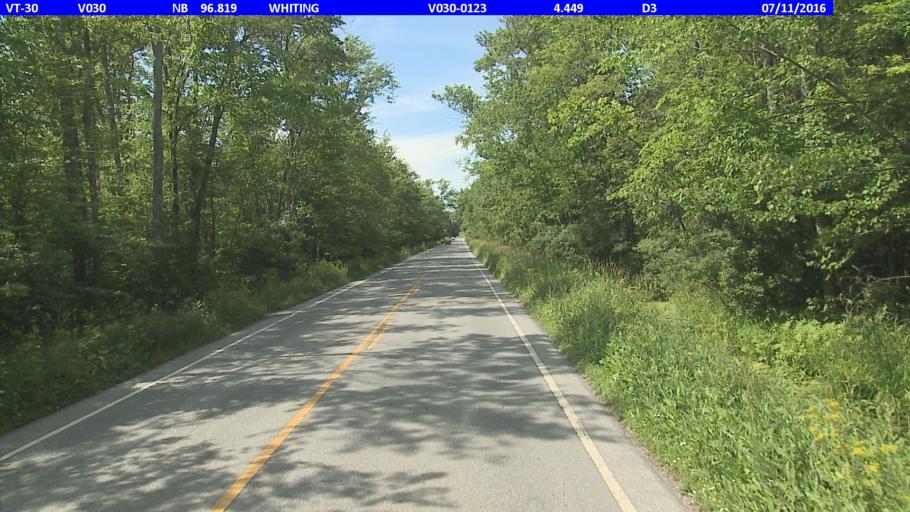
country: US
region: Vermont
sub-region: Addison County
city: Middlebury (village)
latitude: 43.9011
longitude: -73.2059
